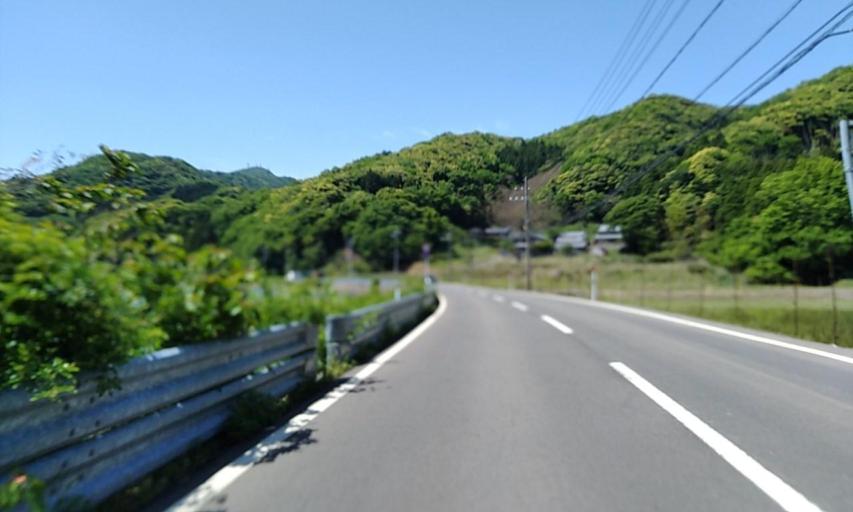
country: JP
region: Fukui
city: Obama
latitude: 35.5367
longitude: 135.7641
